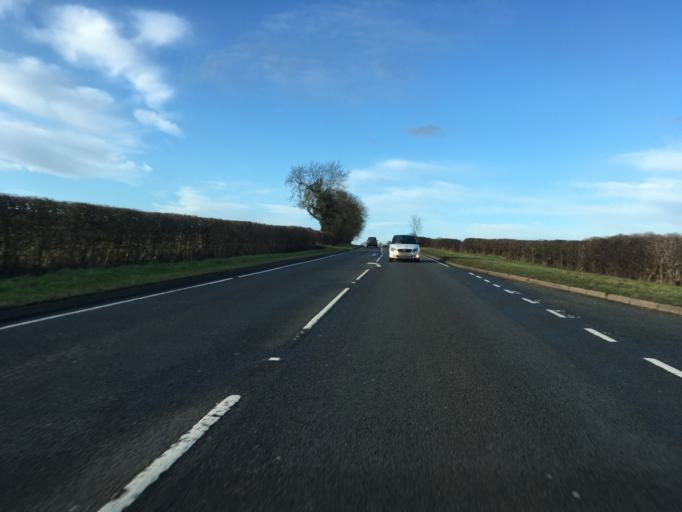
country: GB
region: England
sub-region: Warwickshire
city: Stratford-upon-Avon
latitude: 52.2190
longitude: -1.7313
